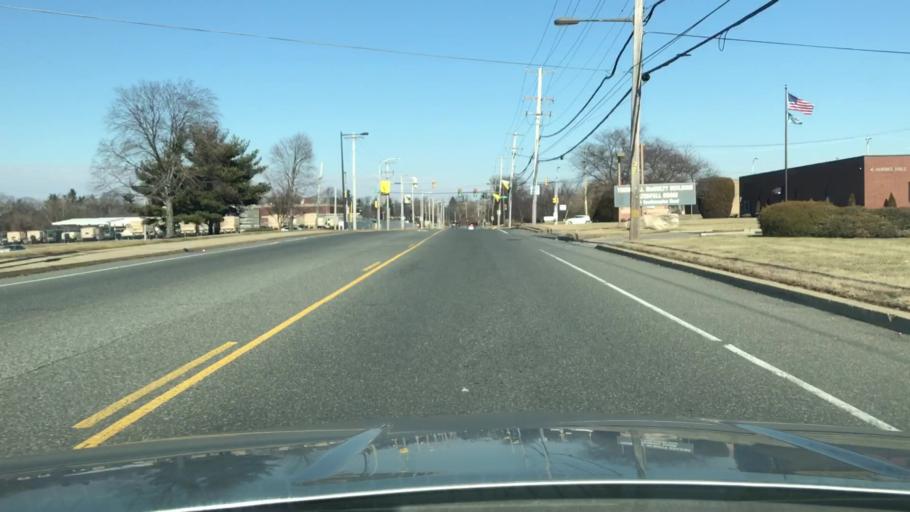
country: US
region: Pennsylvania
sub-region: Bucks County
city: Trevose
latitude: 40.1085
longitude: -74.9868
